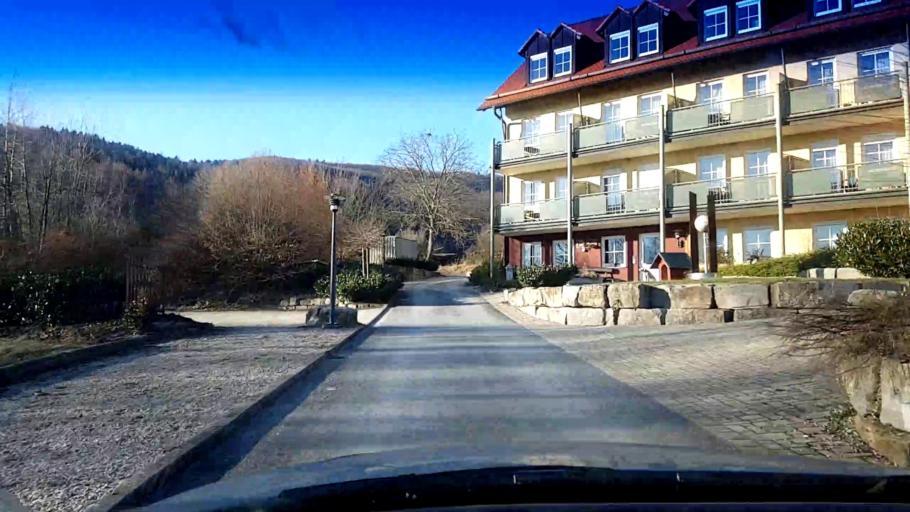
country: DE
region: Bavaria
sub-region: Upper Franconia
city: Litzendorf
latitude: 49.9203
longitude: 11.0470
